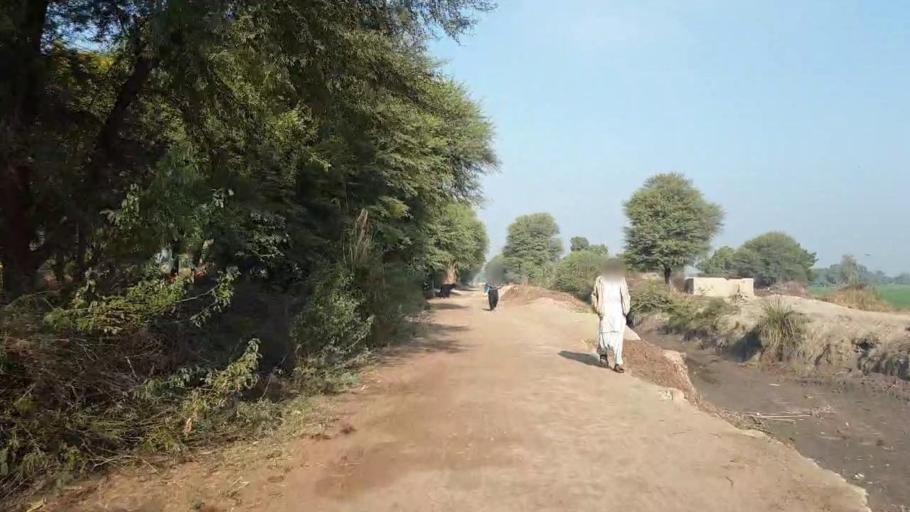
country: PK
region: Sindh
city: Shahdadpur
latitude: 25.9690
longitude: 68.6157
